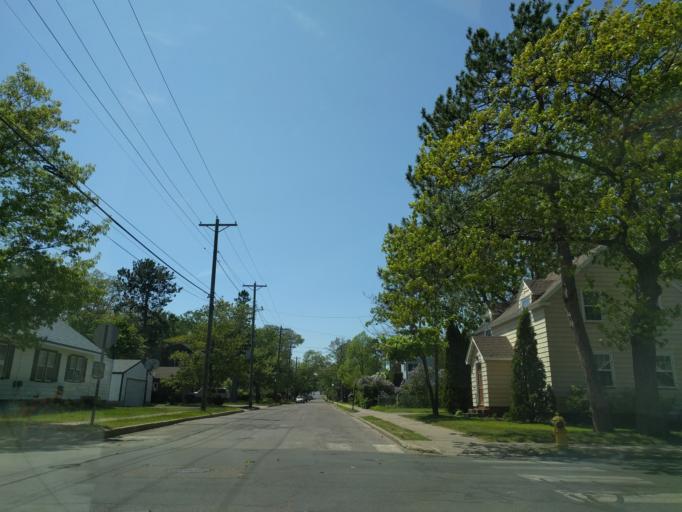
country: US
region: Michigan
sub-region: Marquette County
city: Marquette
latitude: 46.5547
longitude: -87.3892
